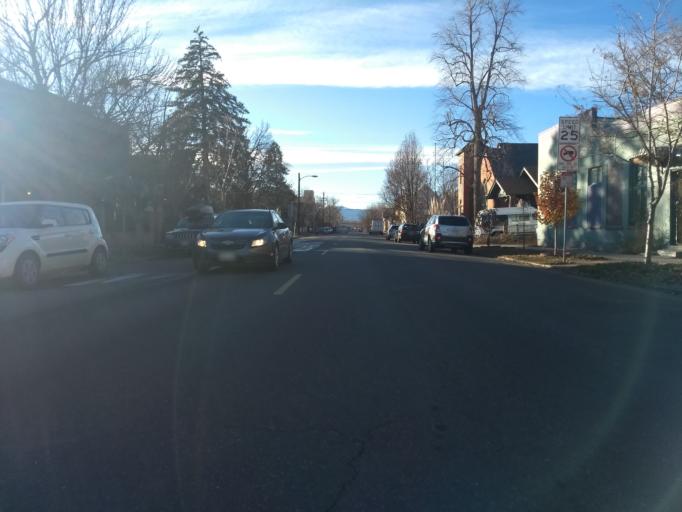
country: US
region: Colorado
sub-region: Denver County
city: Denver
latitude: 39.7184
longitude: -104.9942
